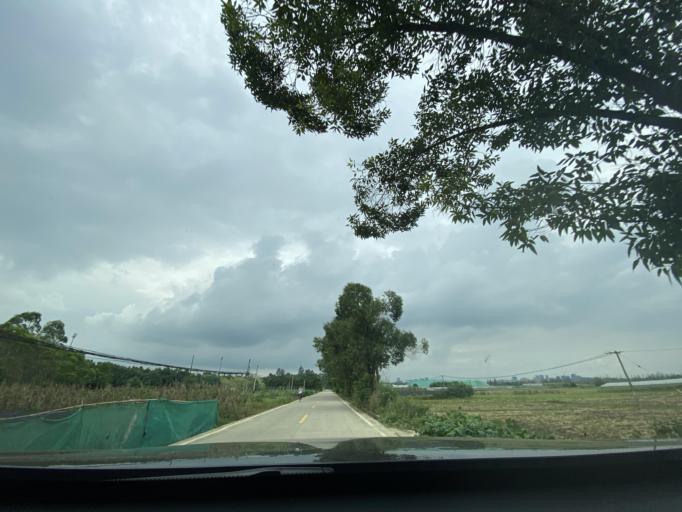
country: CN
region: Sichuan
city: Wujin
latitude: 30.3877
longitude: 103.9673
